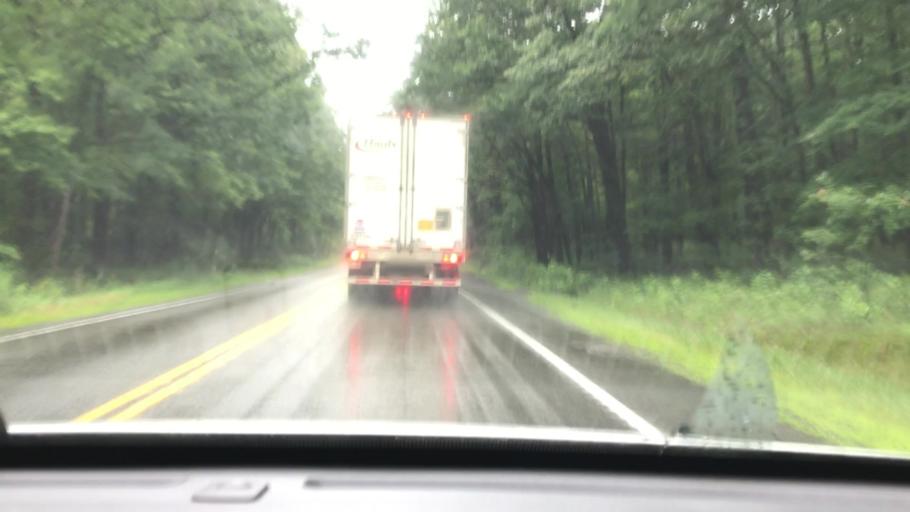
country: US
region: Pennsylvania
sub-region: Clearfield County
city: Osceola Mills
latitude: 40.7846
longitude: -78.2396
